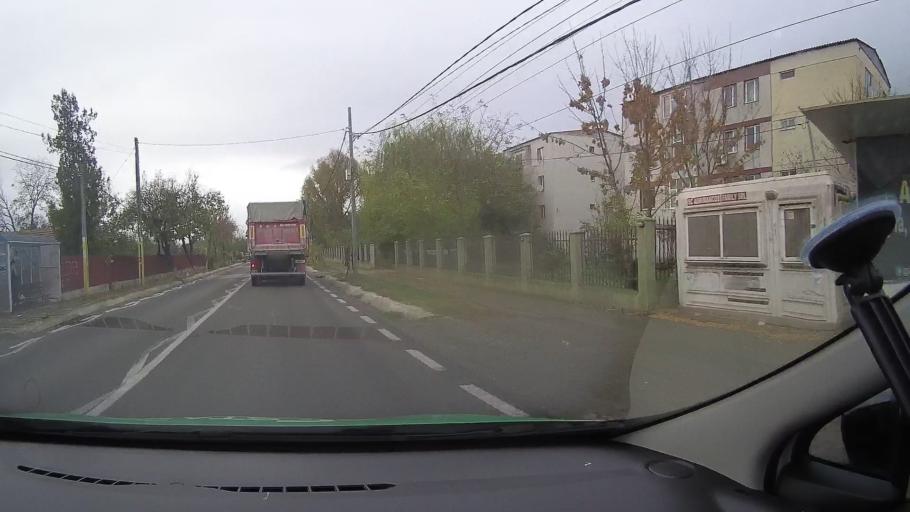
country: RO
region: Constanta
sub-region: Comuna Poarta Alba
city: Poarta Alba
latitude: 44.2071
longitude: 28.3948
